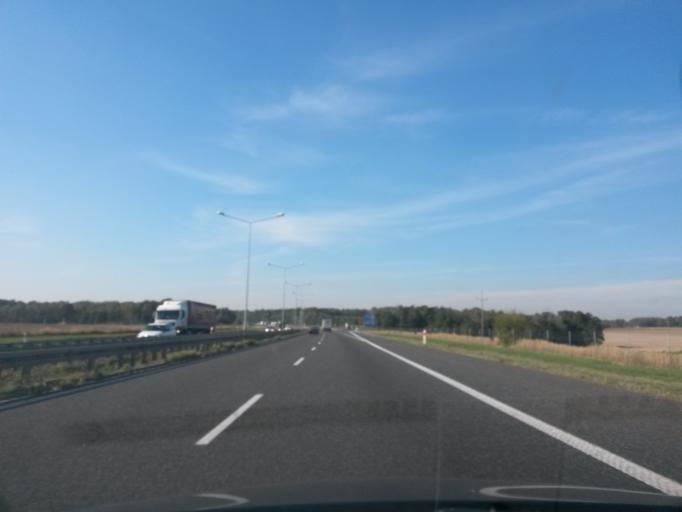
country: PL
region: Opole Voivodeship
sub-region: Powiat strzelecki
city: Ujazd
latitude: 50.4208
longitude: 18.3980
